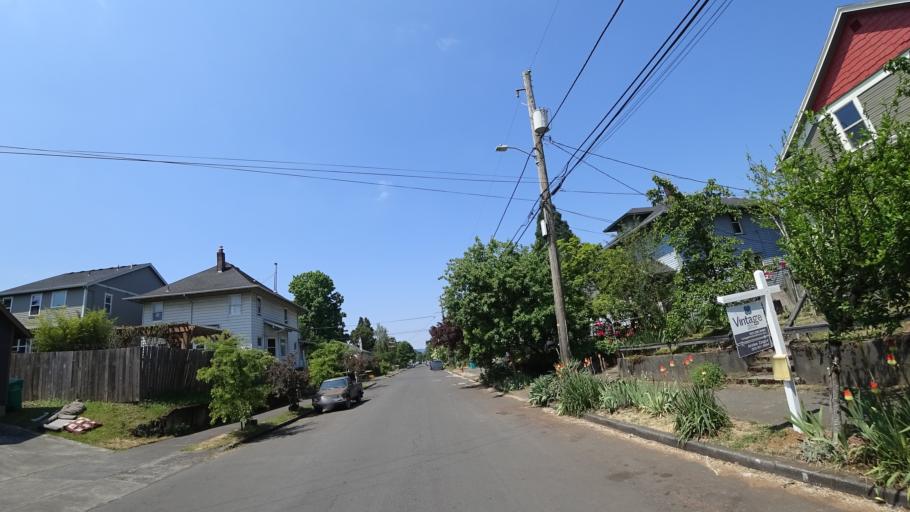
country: US
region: Oregon
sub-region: Multnomah County
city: Portland
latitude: 45.5600
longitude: -122.6549
